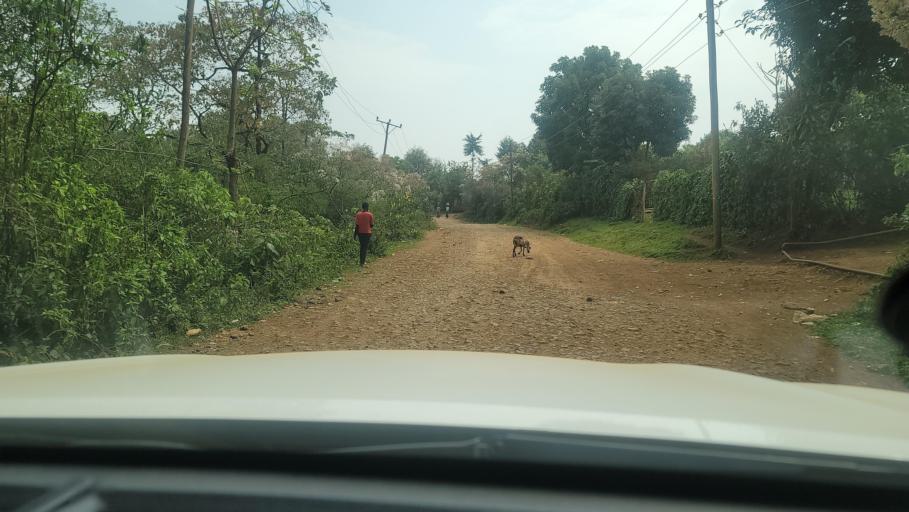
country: ET
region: Oromiya
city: Agaro
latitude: 7.8100
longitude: 36.4714
